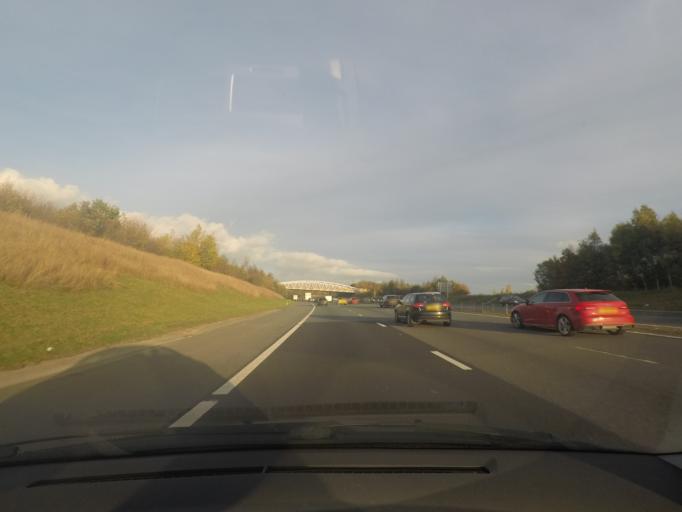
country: GB
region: England
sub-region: City and Borough of Leeds
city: Swillington
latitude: 53.7741
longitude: -1.4440
